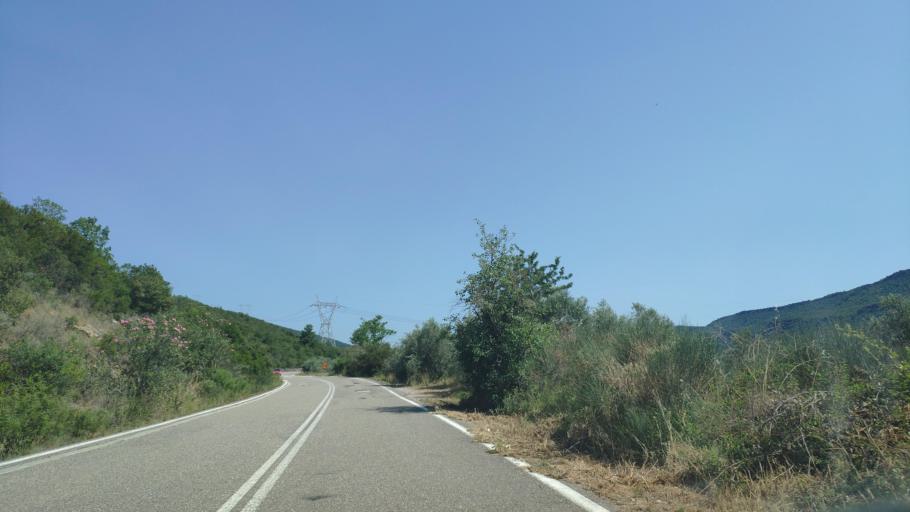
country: GR
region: West Greece
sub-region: Nomos Aitolias kai Akarnanias
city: Lepenou
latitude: 38.7509
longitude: 21.3421
